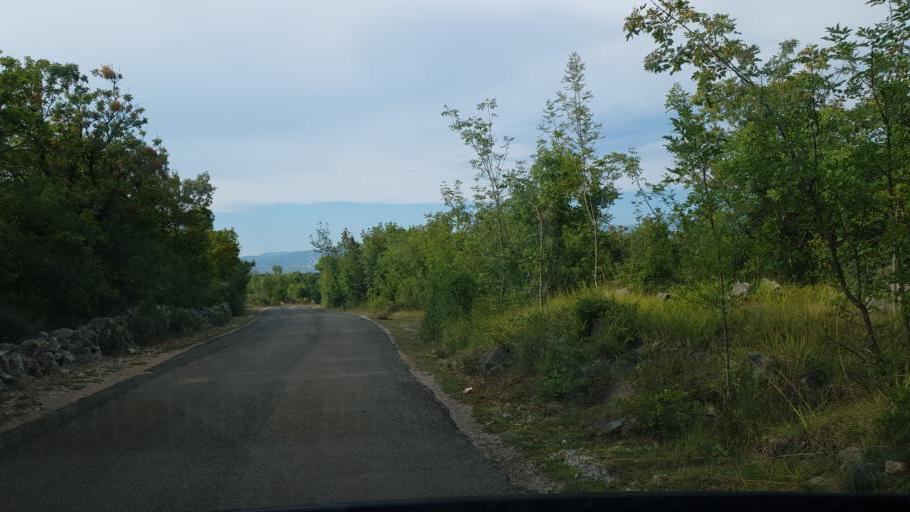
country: HR
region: Primorsko-Goranska
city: Omisalj
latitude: 45.1672
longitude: 14.6059
